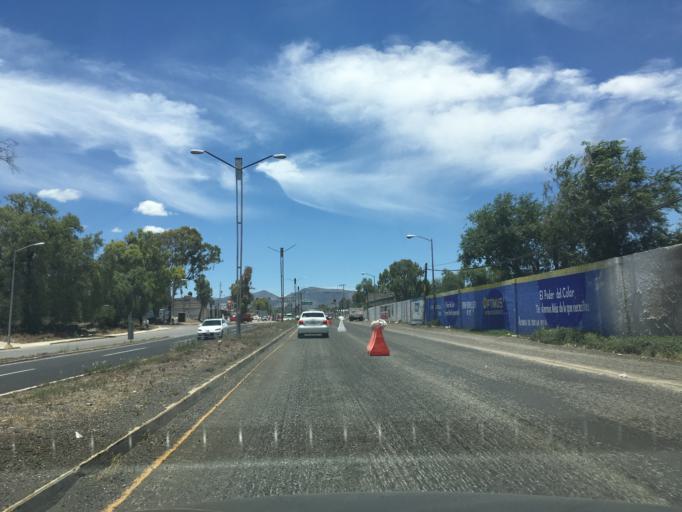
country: MX
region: Hidalgo
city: Actopan
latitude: 20.2549
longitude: -98.9364
